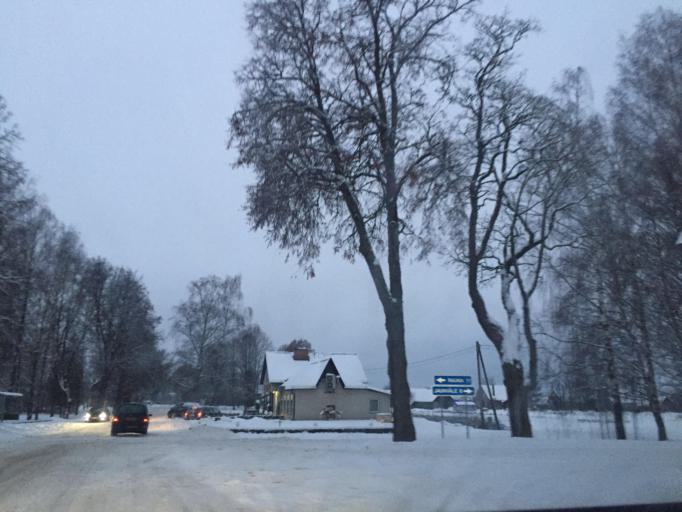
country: LV
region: Raunas
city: Rauna
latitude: 57.4218
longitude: 25.5812
